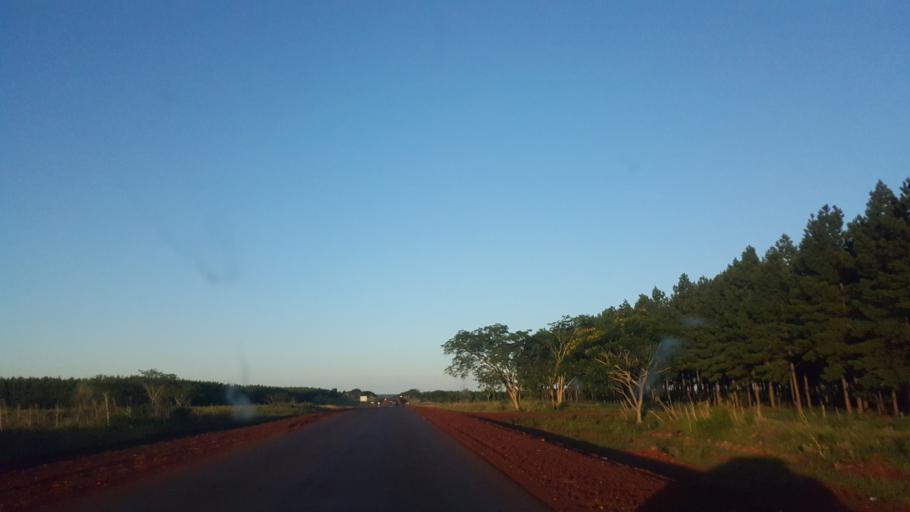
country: AR
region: Corrientes
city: Santo Tome
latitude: -28.5003
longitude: -56.0529
